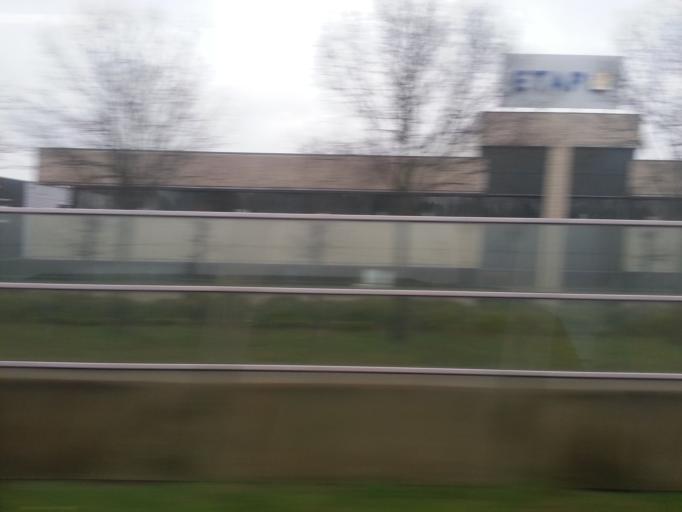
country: NL
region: North Brabant
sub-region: Gemeente Breda
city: Breda
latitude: 51.6098
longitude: 4.7186
